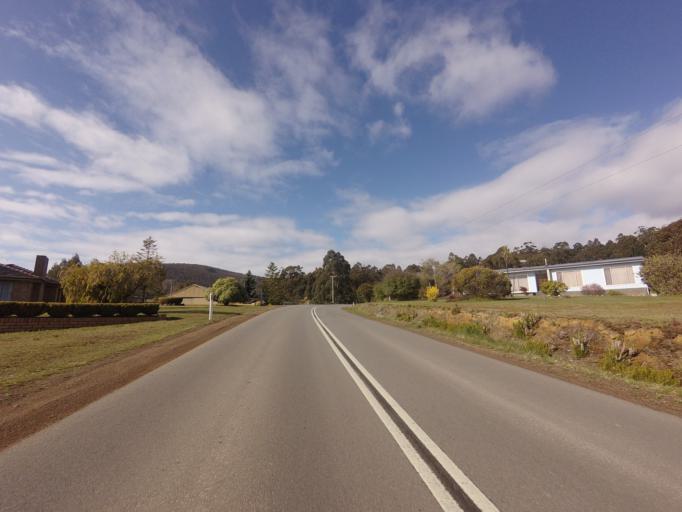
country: AU
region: Tasmania
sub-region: Huon Valley
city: Geeveston
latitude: -43.3383
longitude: 146.9714
